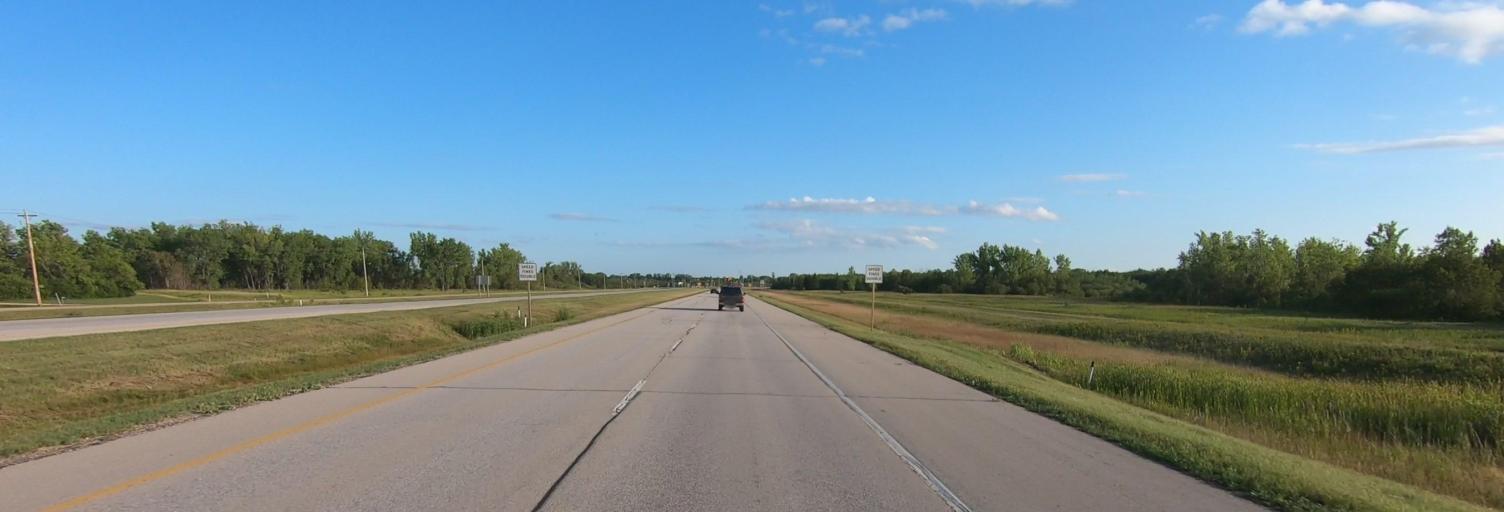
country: CA
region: Manitoba
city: Selkirk
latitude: 49.9809
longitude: -96.9746
